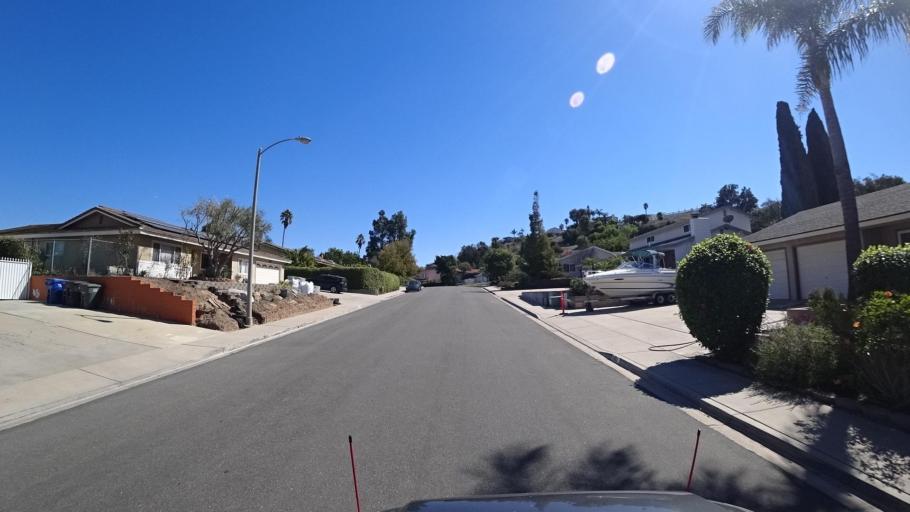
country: US
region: California
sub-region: San Diego County
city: Bonita
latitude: 32.6635
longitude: -117.0187
